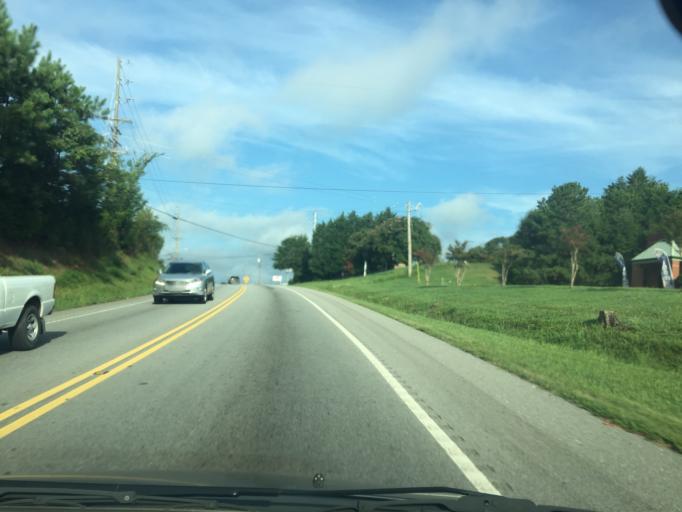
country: US
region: Tennessee
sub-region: Hamilton County
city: Harrison
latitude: 35.0746
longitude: -85.1666
